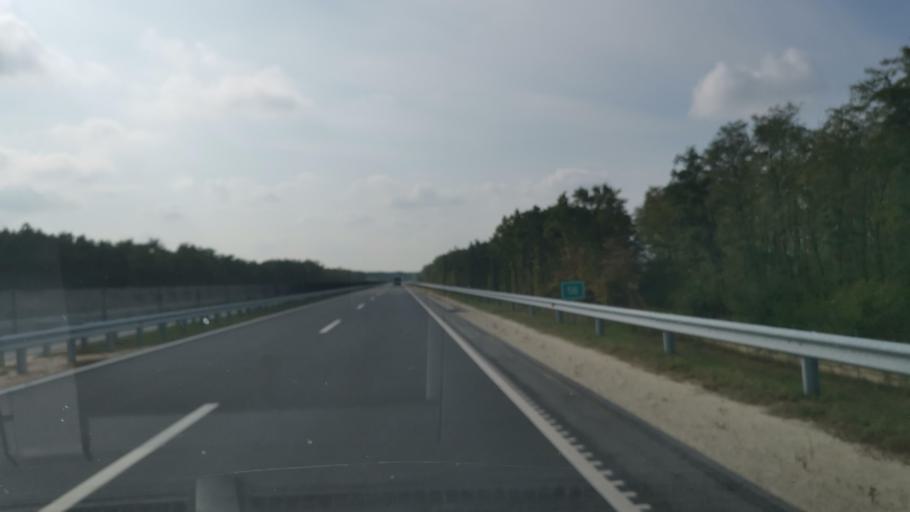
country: HU
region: Gyor-Moson-Sopron
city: Fertoszentmiklos
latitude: 47.5653
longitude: 16.8985
